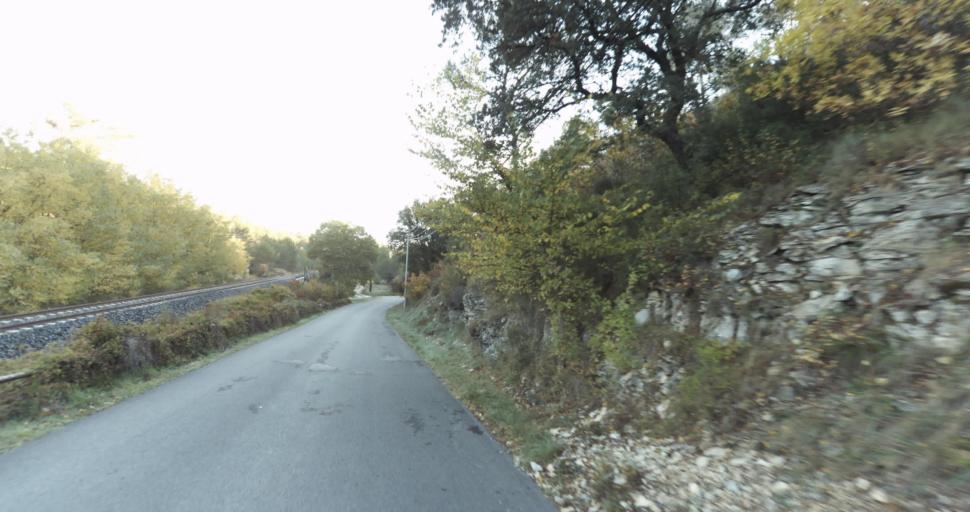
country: FR
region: Provence-Alpes-Cote d'Azur
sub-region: Departement des Bouches-du-Rhone
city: Venelles
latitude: 43.5884
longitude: 5.5084
